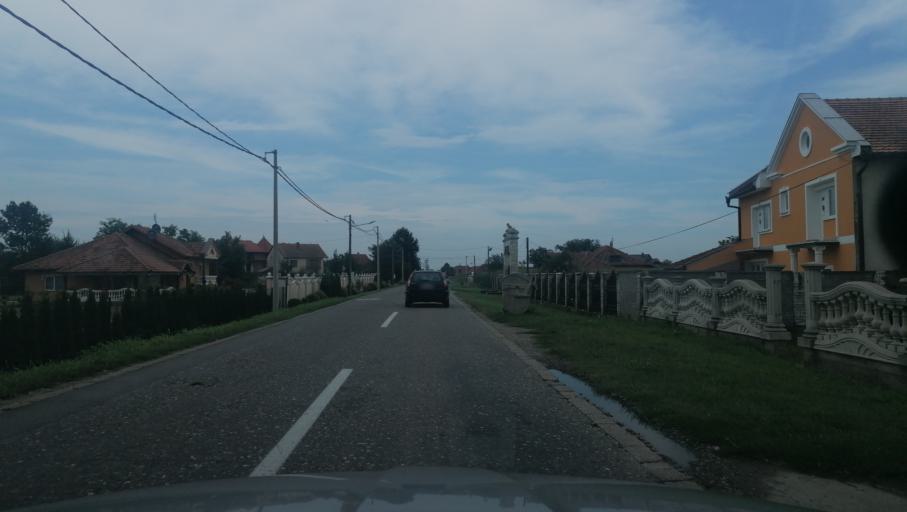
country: RS
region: Central Serbia
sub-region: Macvanski Okrug
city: Bogatic
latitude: 44.8274
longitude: 19.4614
